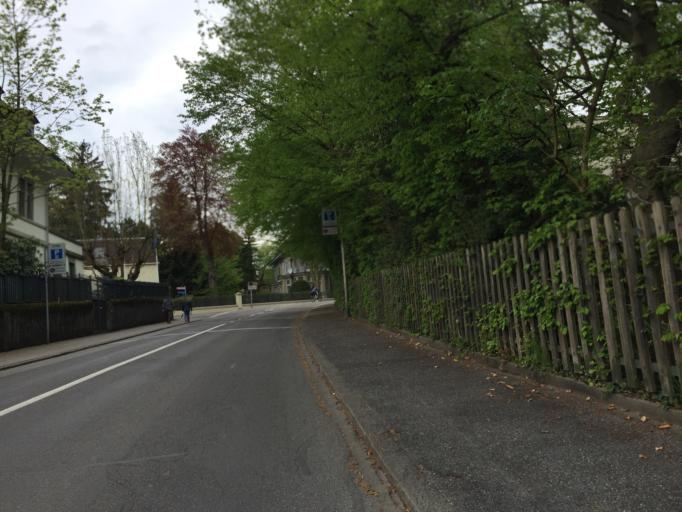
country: CH
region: Bern
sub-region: Bern-Mittelland District
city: Bern
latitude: 46.9378
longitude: 7.4633
